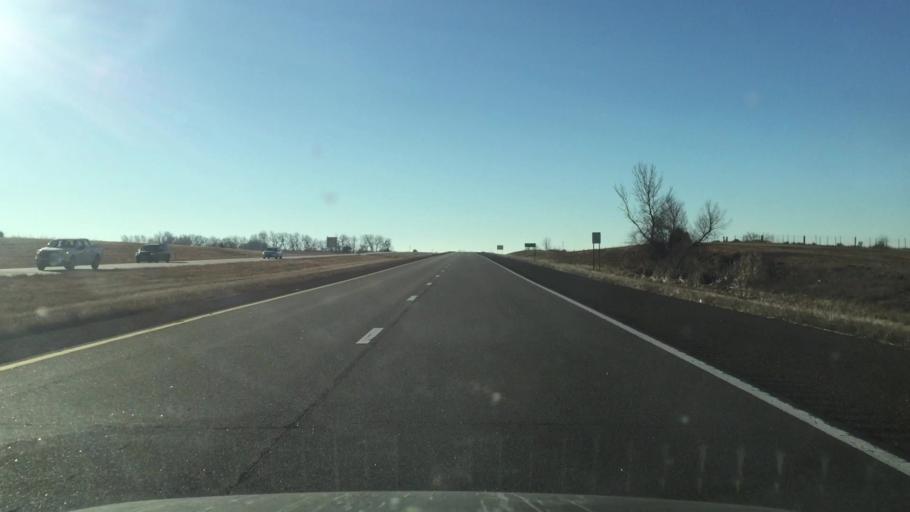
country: US
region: Kansas
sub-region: Miami County
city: Paola
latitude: 38.6144
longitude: -94.8359
